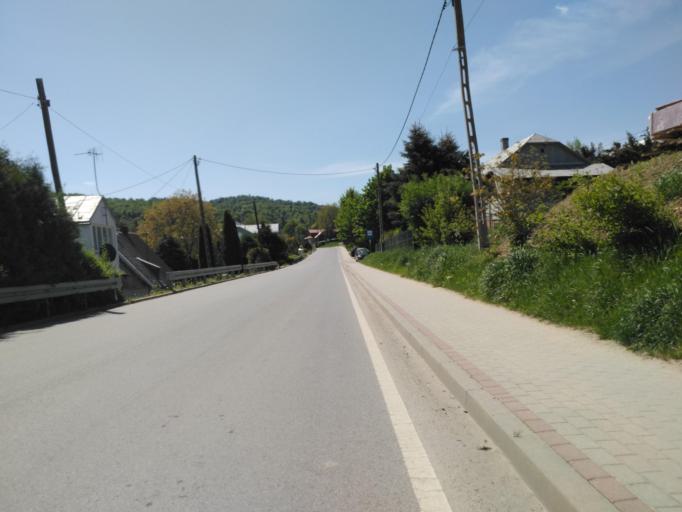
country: PL
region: Subcarpathian Voivodeship
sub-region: Powiat krosnienski
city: Iwonicz-Zdroj
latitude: 49.5730
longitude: 21.7928
